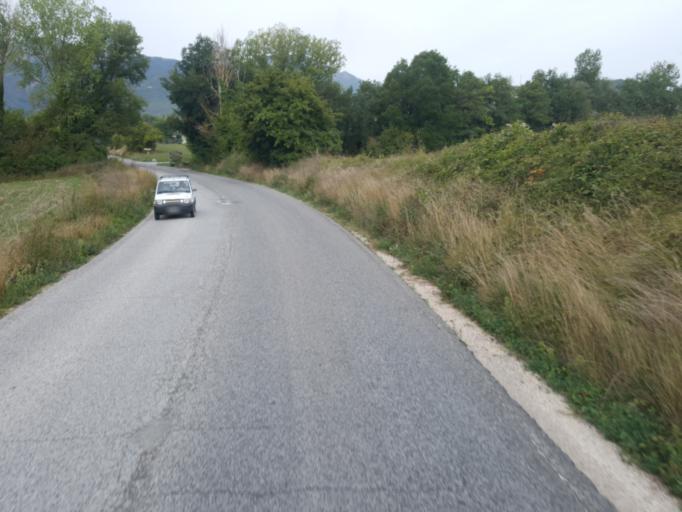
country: IT
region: The Marches
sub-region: Provincia di Ancona
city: Fabriano
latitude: 43.3471
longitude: 12.8445
